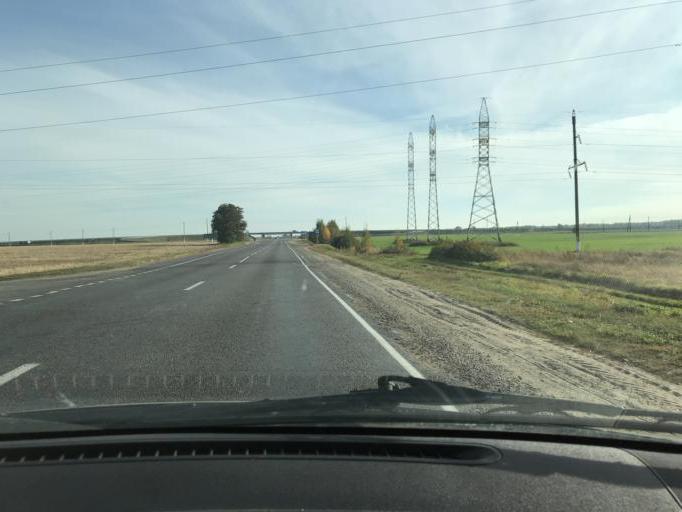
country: BY
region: Brest
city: Asnyezhytsy
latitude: 52.1900
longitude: 26.0751
